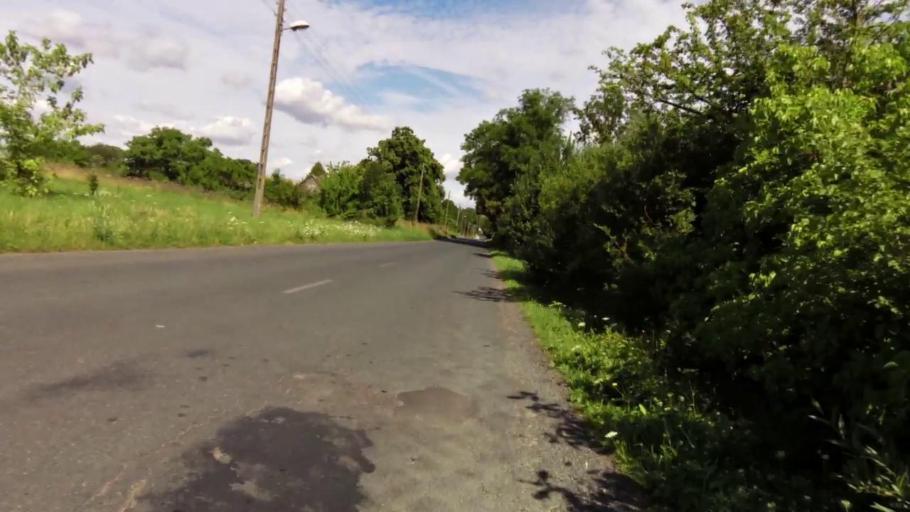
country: PL
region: West Pomeranian Voivodeship
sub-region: Powiat stargardzki
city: Dobrzany
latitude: 53.4064
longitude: 15.4306
